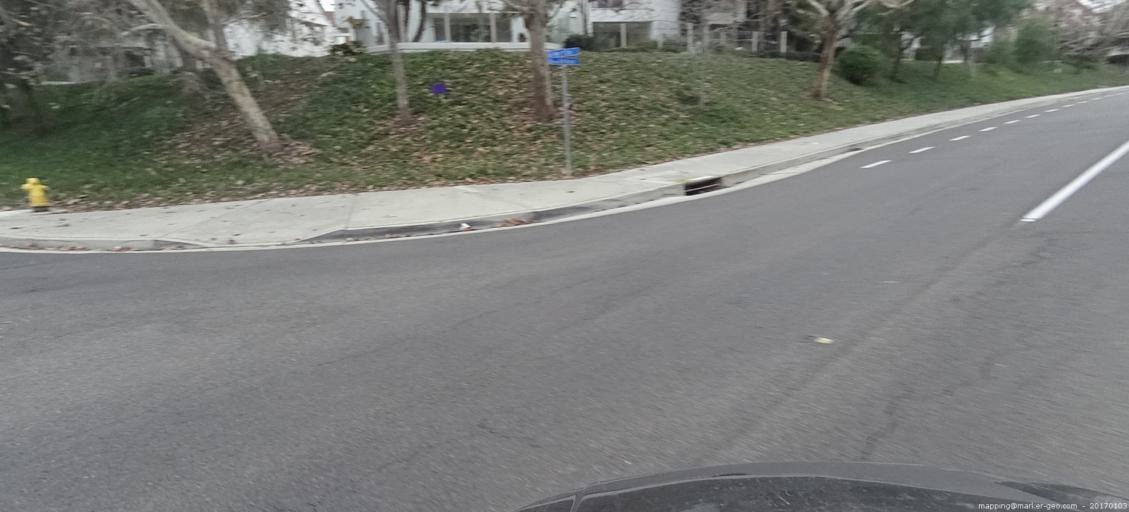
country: US
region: California
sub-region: Orange County
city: Dana Point
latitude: 33.4895
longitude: -117.6932
